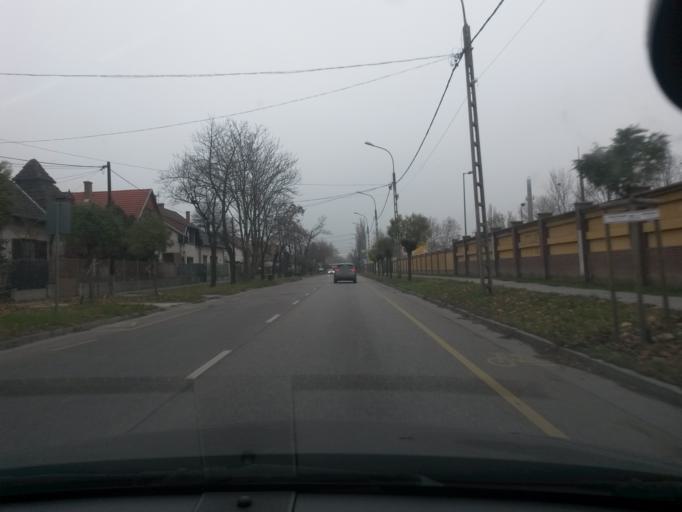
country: HU
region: Budapest
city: Budapest XV. keruelet
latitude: 47.5718
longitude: 19.1069
